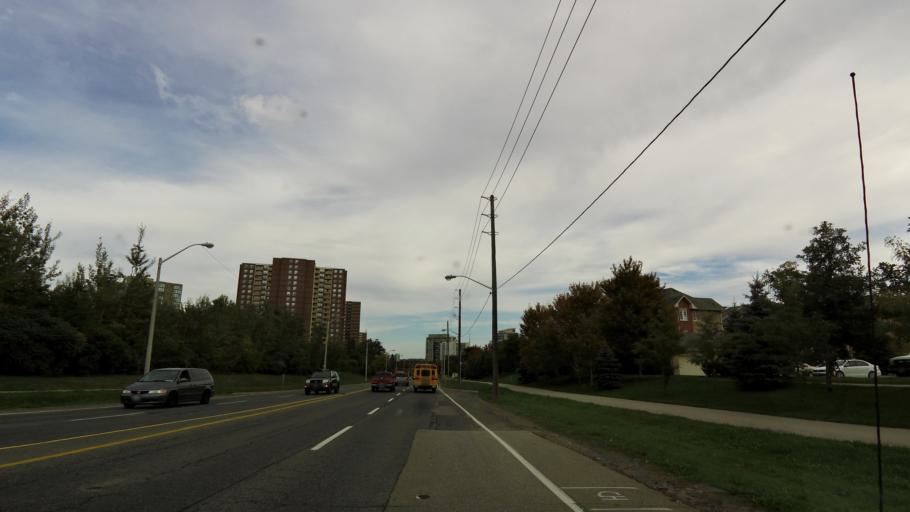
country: CA
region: Ontario
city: Etobicoke
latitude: 43.6833
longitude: -79.5197
